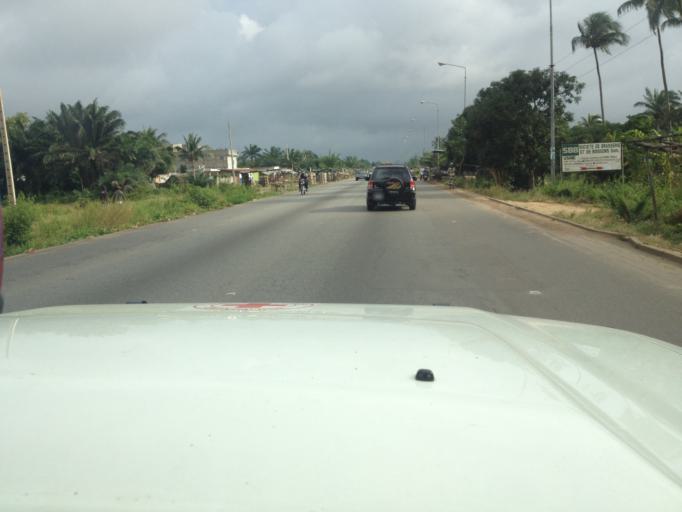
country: BJ
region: Queme
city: Porto-Novo
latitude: 6.4382
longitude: 2.6236
